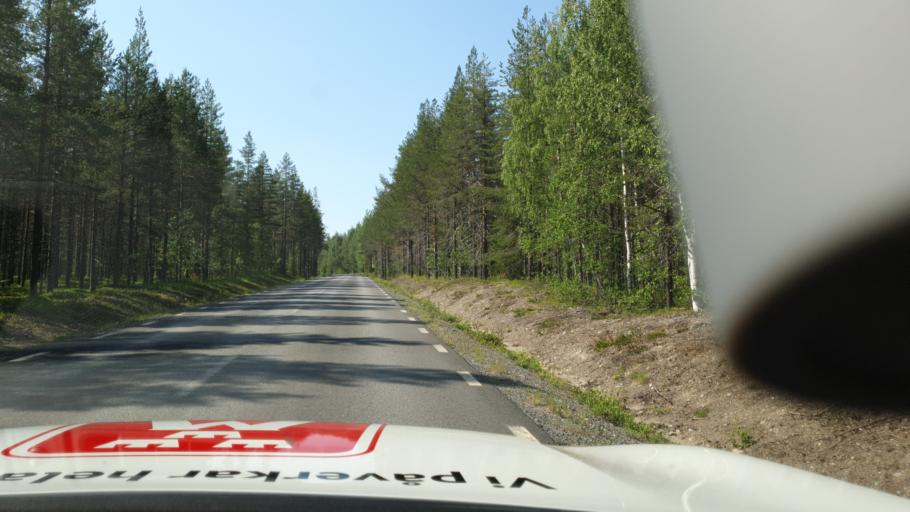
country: SE
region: Vaesterbotten
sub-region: Skelleftea Kommun
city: Langsele
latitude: 64.9771
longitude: 20.0565
